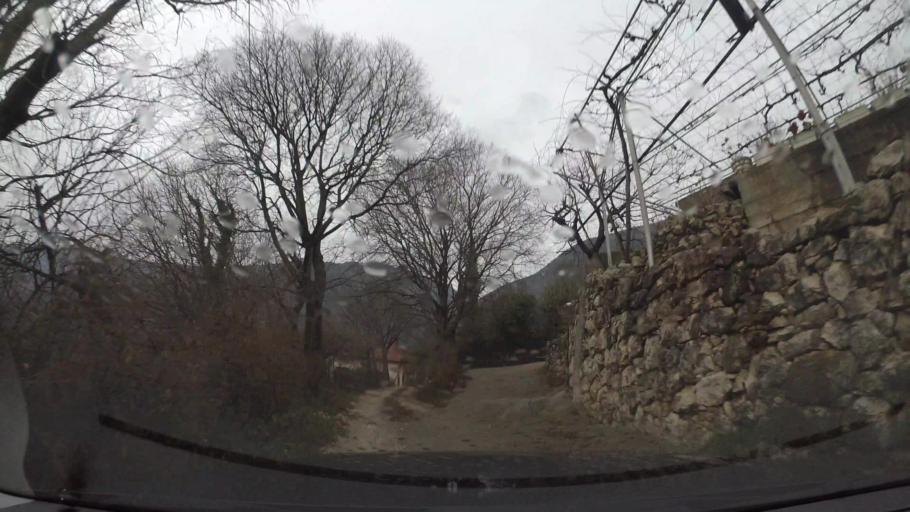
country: BA
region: Federation of Bosnia and Herzegovina
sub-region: Hercegovacko-Bosanski Kanton
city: Mostar
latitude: 43.3697
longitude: 17.8099
